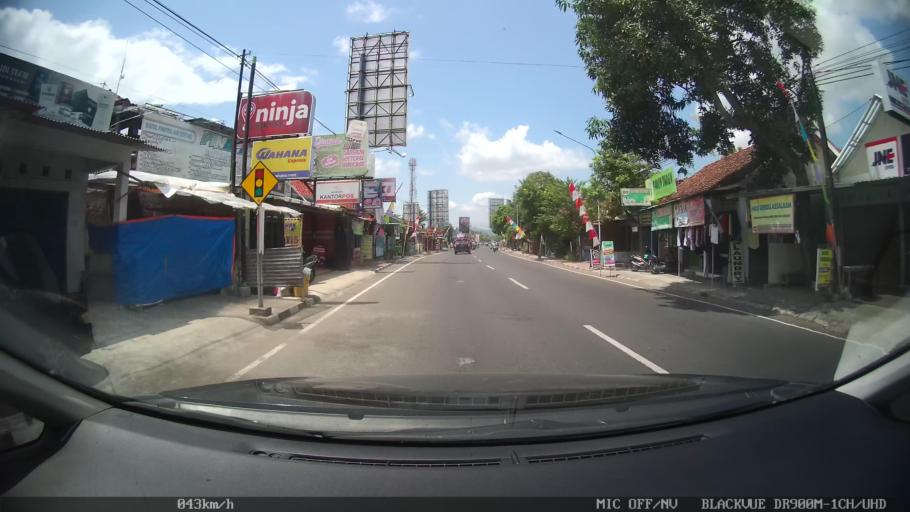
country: ID
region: Daerah Istimewa Yogyakarta
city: Bantul
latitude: -7.8925
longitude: 110.3336
